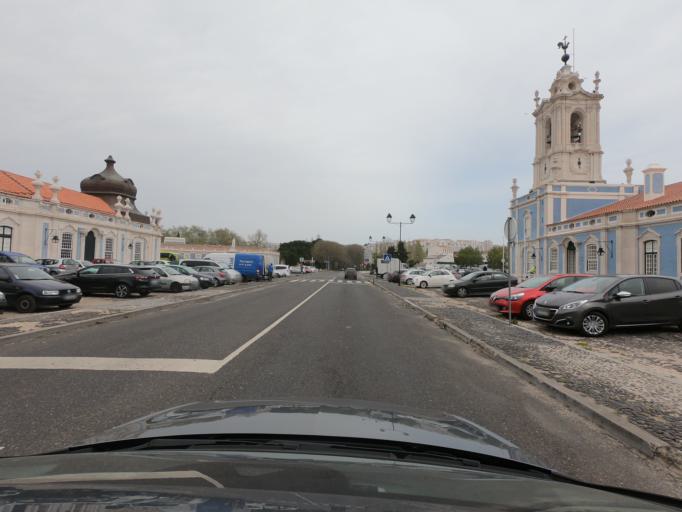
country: PT
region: Lisbon
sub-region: Sintra
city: Queluz
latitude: 38.7505
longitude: -9.2577
